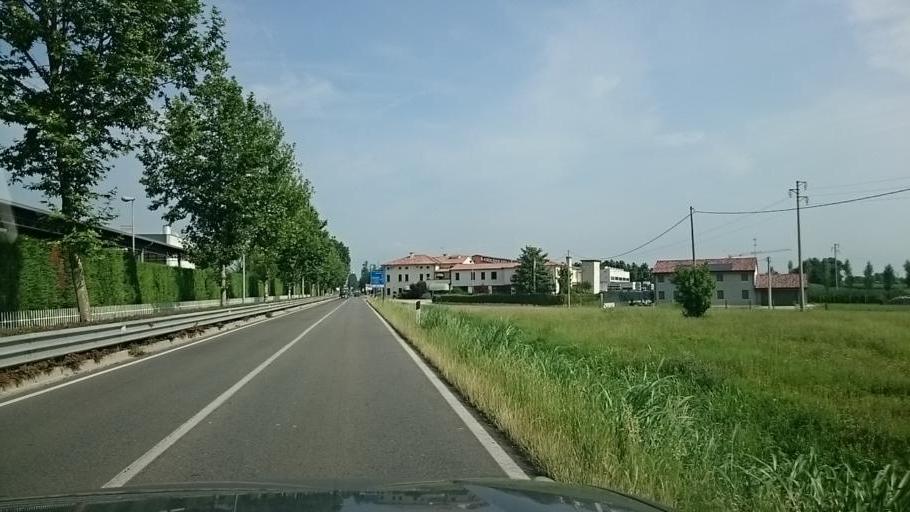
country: IT
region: Veneto
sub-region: Provincia di Treviso
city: Castelfranco Veneto
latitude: 45.6535
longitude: 11.9421
